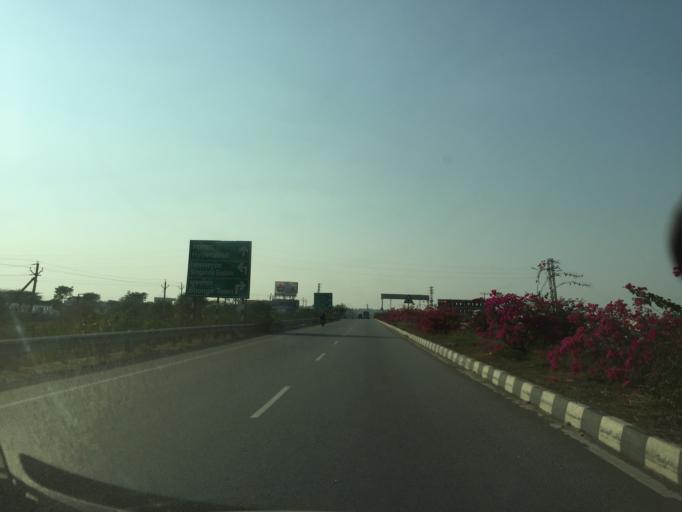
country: IN
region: Telangana
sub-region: Nalgonda
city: Bhongir
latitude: 17.5004
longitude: 78.8857
